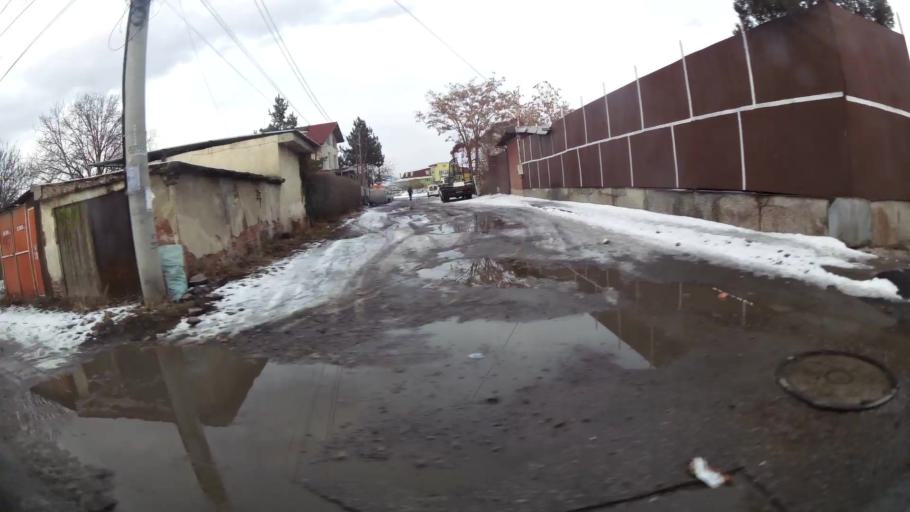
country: BG
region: Sofia-Capital
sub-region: Stolichna Obshtina
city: Sofia
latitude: 42.7233
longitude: 23.3478
